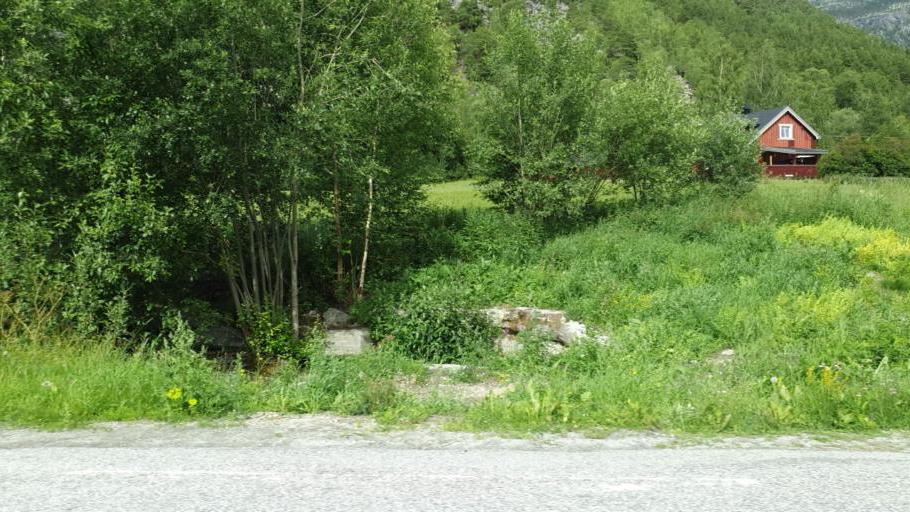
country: NO
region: Oppland
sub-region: Sel
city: Otta
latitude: 61.8416
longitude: 9.3993
